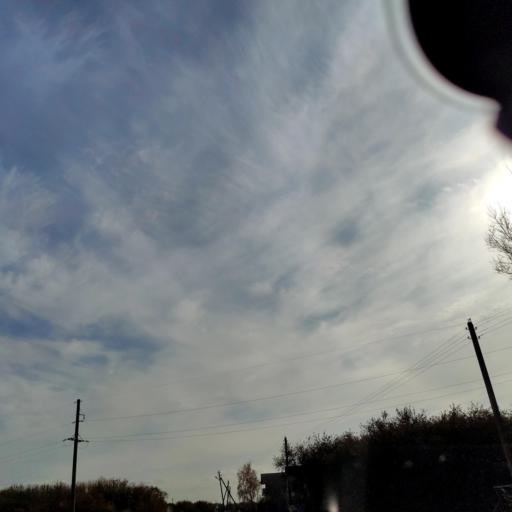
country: RU
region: Voronezj
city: Rossosh'
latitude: 51.1948
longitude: 38.7794
